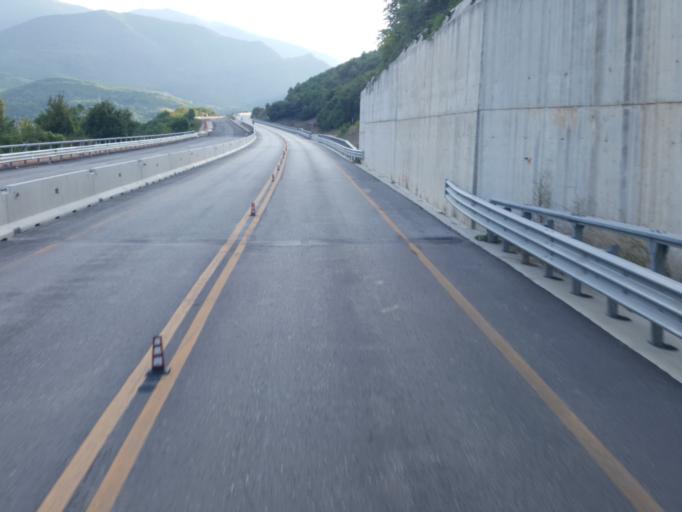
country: IT
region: The Marches
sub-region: Provincia di Ancona
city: Fabriano
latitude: 43.3075
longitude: 12.8459
